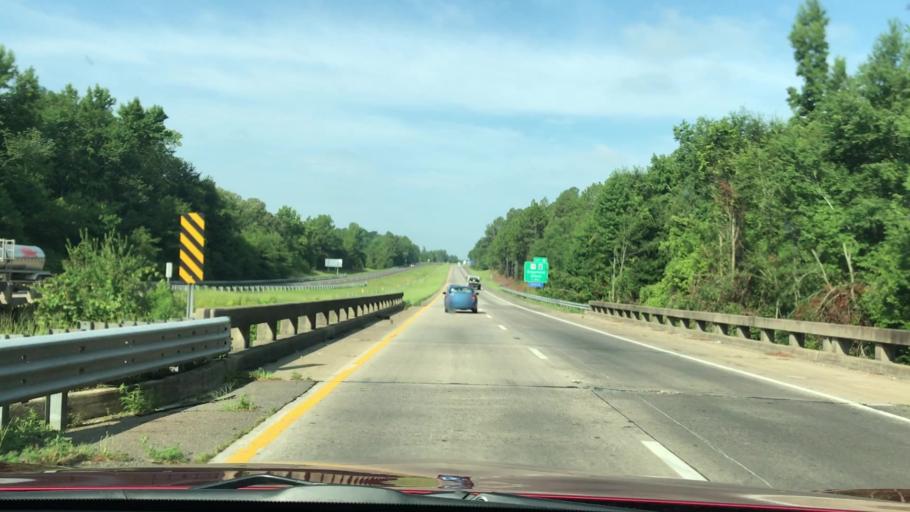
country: US
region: South Carolina
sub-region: Aiken County
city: Aiken
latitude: 33.6477
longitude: -81.7194
